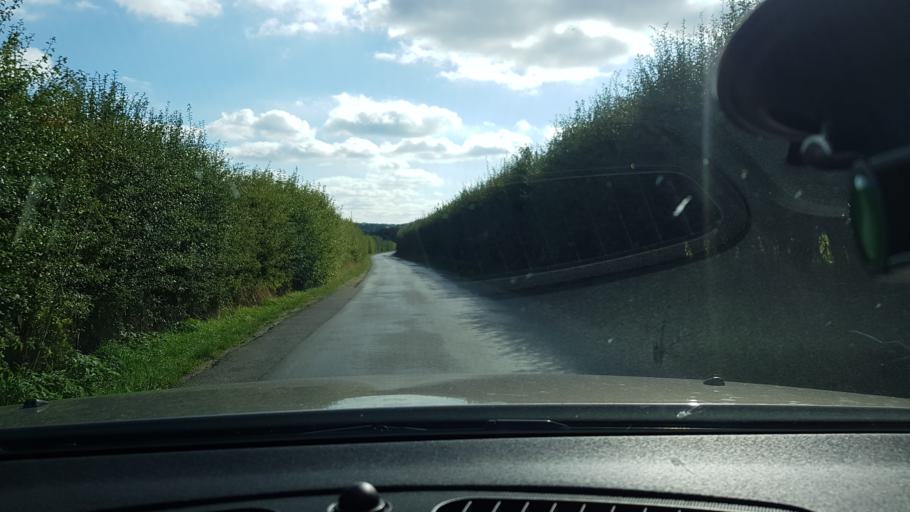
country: GB
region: England
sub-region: West Berkshire
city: Kintbury
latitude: 51.4182
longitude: -1.4464
